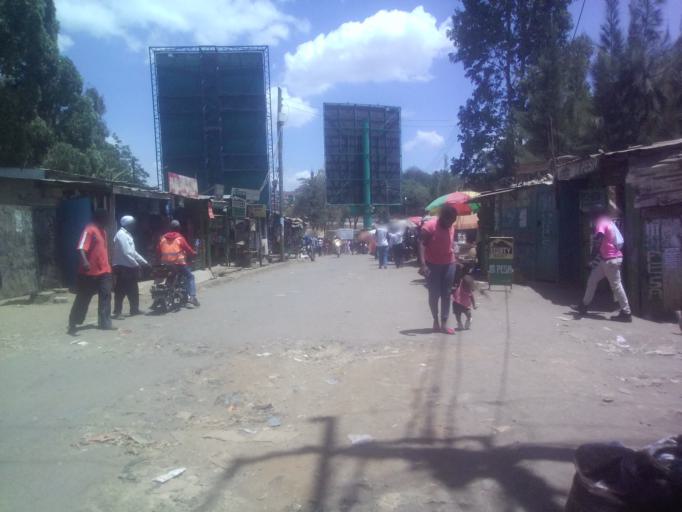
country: KE
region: Nairobi Area
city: Nairobi
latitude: -1.3065
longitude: 36.7875
